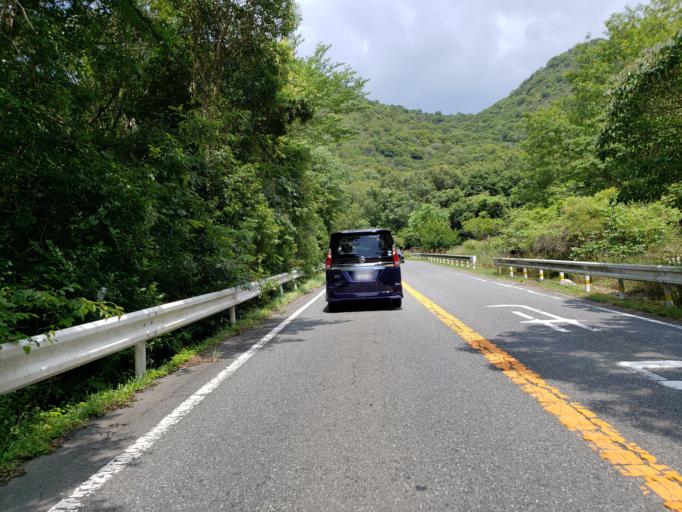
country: JP
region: Hyogo
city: Aioi
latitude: 34.7770
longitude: 134.4346
